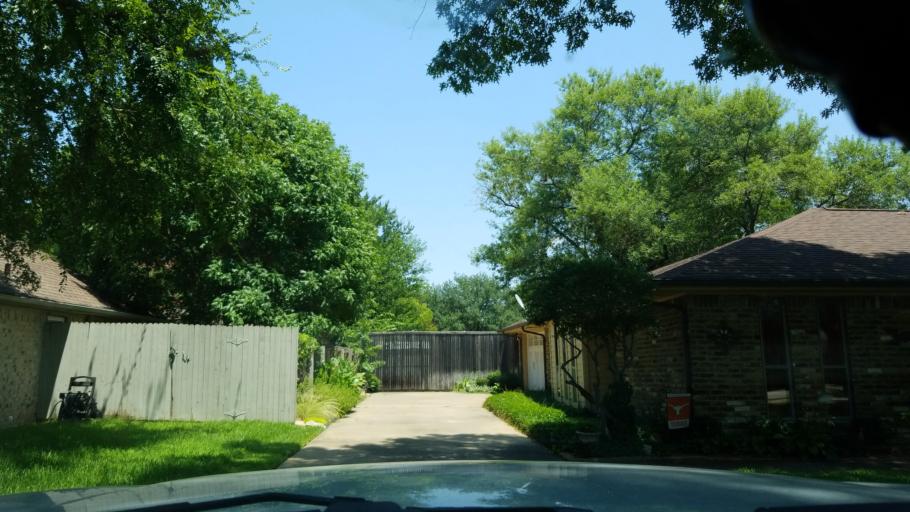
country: US
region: Texas
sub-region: Dallas County
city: Coppell
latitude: 32.9595
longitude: -96.9887
